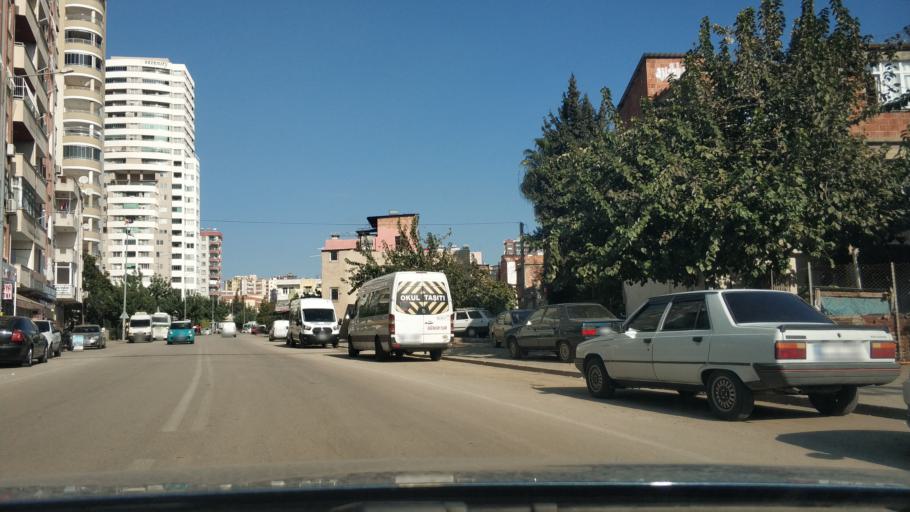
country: TR
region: Adana
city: Seyhan
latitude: 37.0191
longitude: 35.2914
